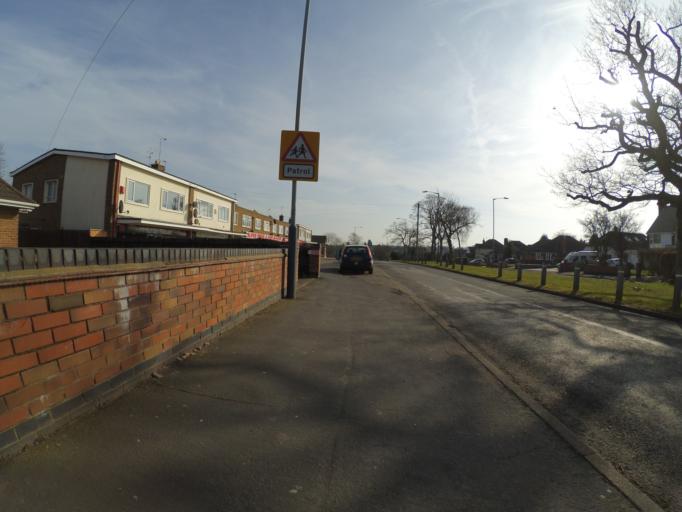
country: GB
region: England
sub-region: Warwickshire
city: Rugby
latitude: 52.3660
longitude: -1.2312
